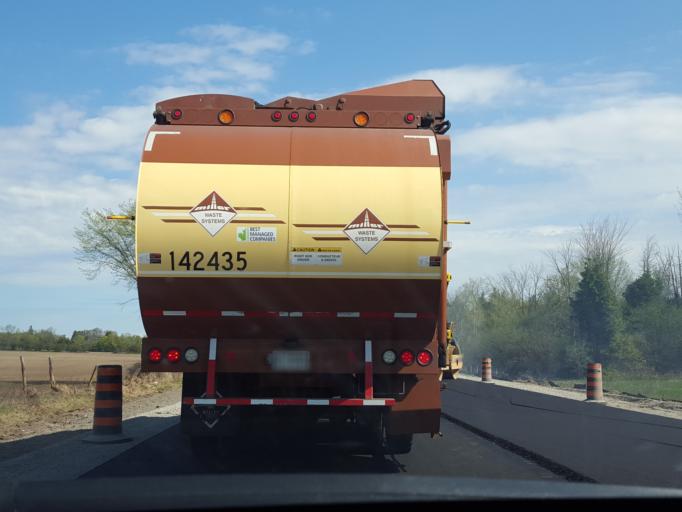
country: CA
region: Ontario
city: Uxbridge
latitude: 44.0753
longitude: -78.9364
